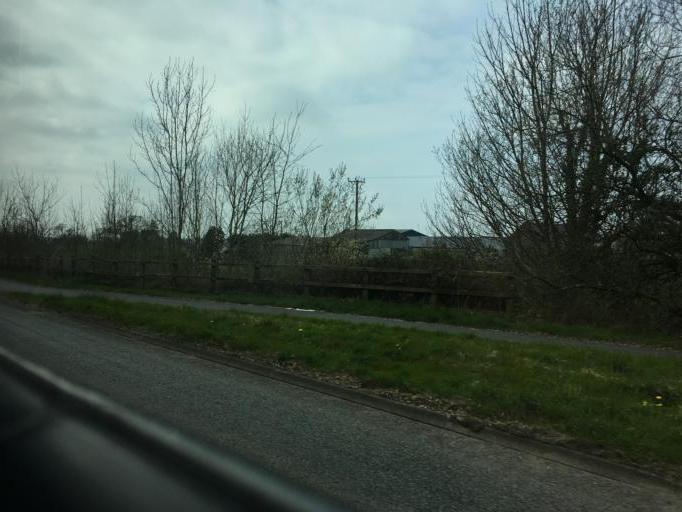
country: GB
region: Wales
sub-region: Gwynedd
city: Y Felinheli
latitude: 53.1713
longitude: -4.2298
